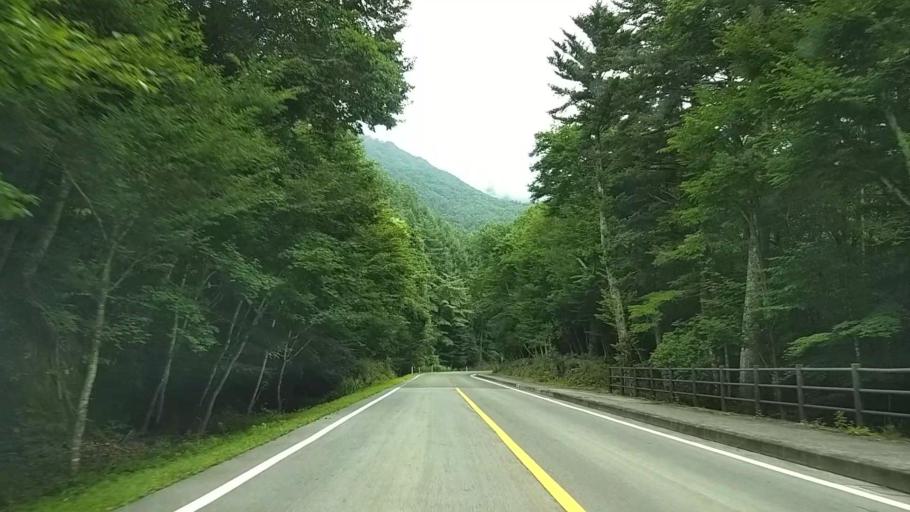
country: JP
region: Yamanashi
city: Fujikawaguchiko
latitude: 35.4953
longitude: 138.6493
